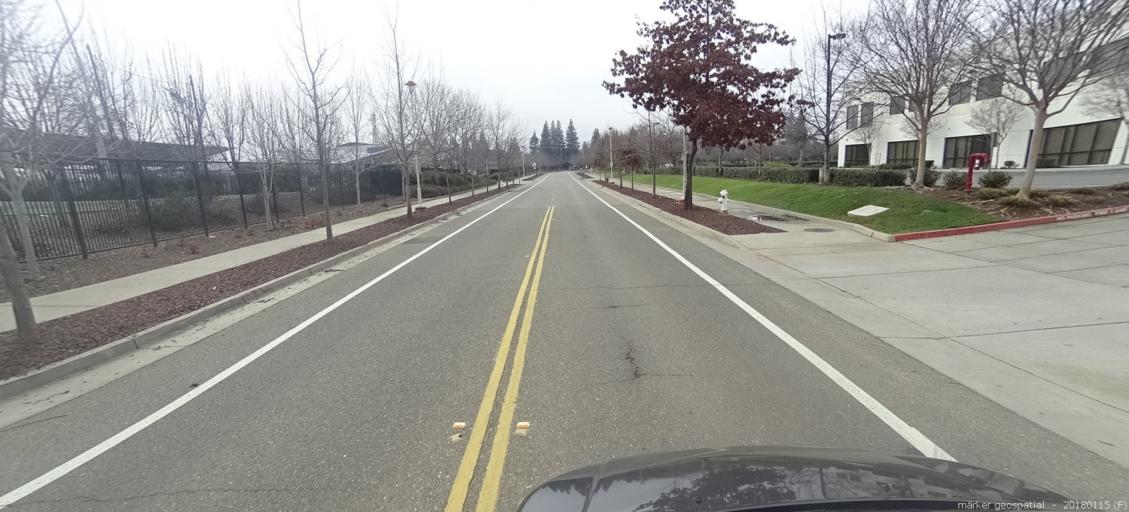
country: US
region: California
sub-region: Sacramento County
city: Rancho Cordova
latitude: 38.5716
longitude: -121.3037
